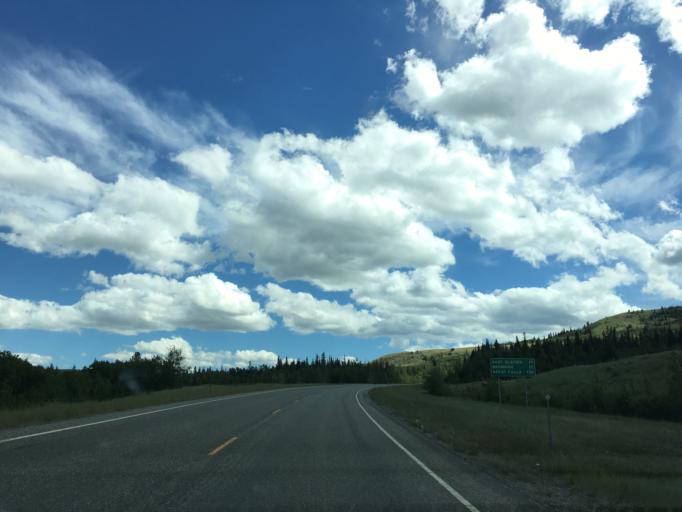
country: US
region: Montana
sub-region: Glacier County
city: Browning
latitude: 48.6073
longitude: -113.2860
